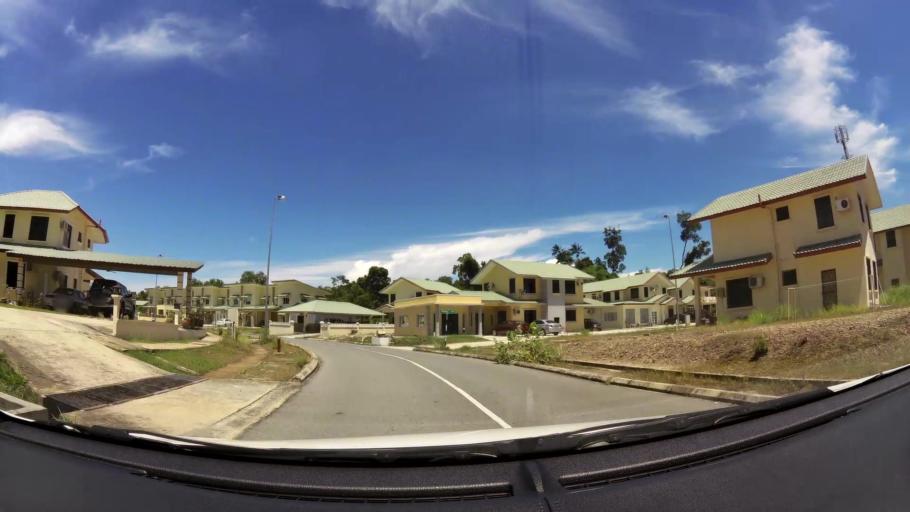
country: BN
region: Brunei and Muara
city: Bandar Seri Begawan
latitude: 5.0292
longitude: 115.0375
